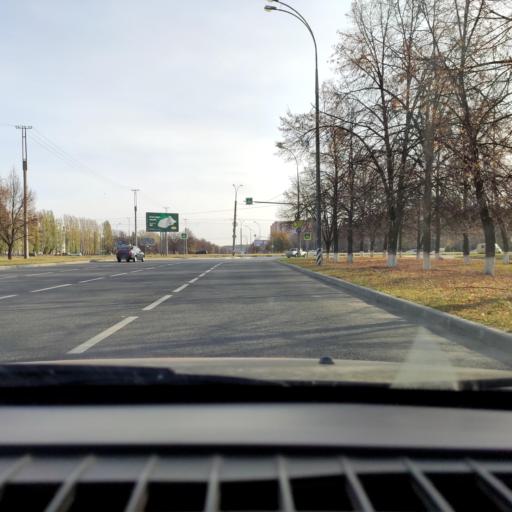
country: RU
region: Samara
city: Tol'yatti
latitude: 53.5184
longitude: 49.2926
